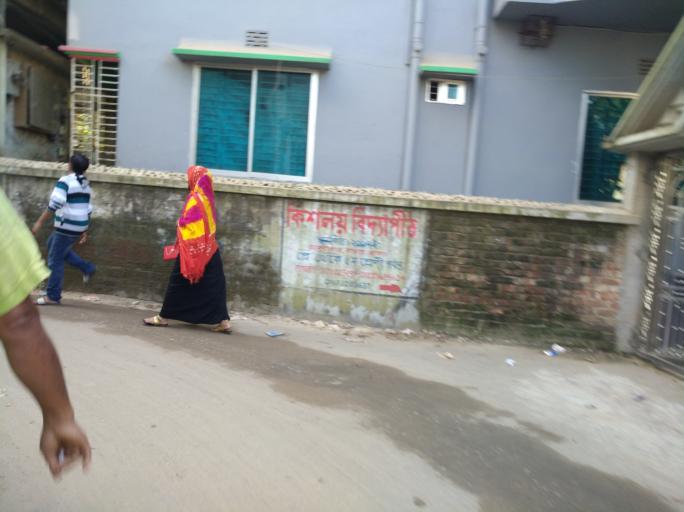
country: BD
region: Dhaka
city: Tungi
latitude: 23.8873
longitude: 90.2643
